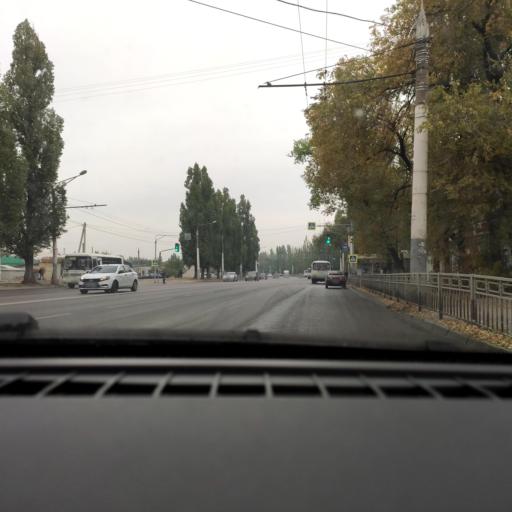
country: RU
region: Voronezj
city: Maslovka
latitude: 51.6159
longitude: 39.2374
